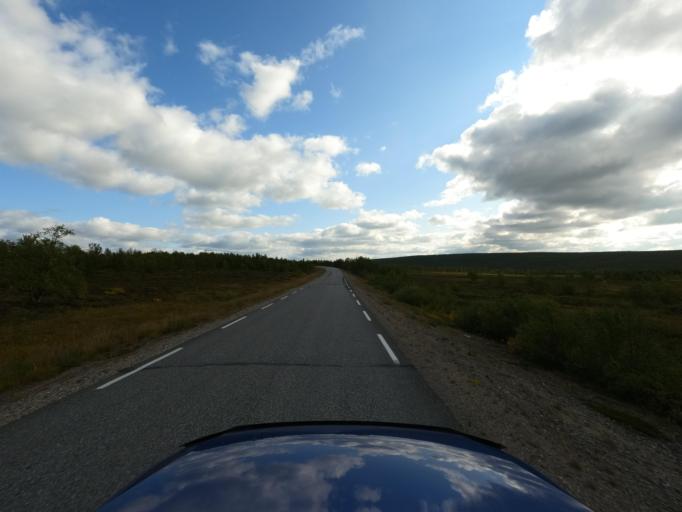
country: NO
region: Finnmark Fylke
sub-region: Porsanger
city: Lakselv
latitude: 69.3737
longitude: 24.4116
